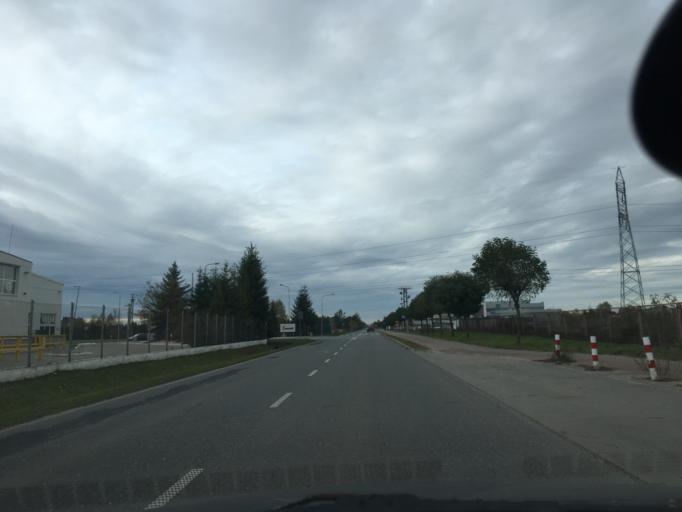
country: PL
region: Masovian Voivodeship
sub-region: Powiat zyrardowski
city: Mszczonow
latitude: 51.9732
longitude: 20.5463
